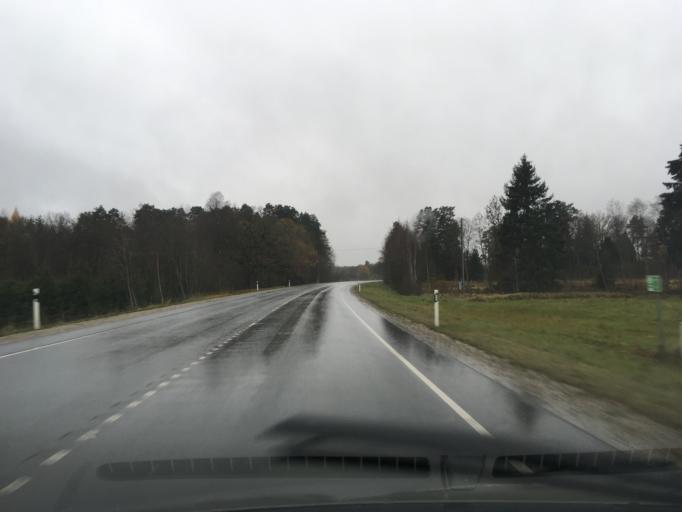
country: EE
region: Harju
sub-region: Nissi vald
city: Turba
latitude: 58.9000
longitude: 24.1079
